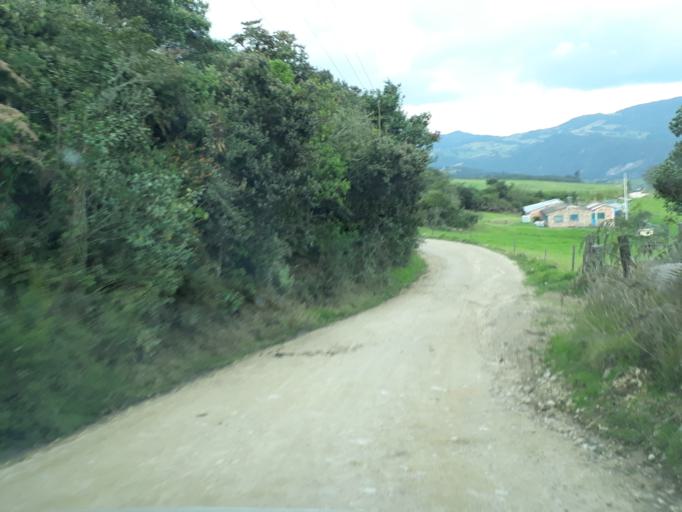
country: CO
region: Cundinamarca
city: Lenguazaque
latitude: 5.2560
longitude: -73.6879
